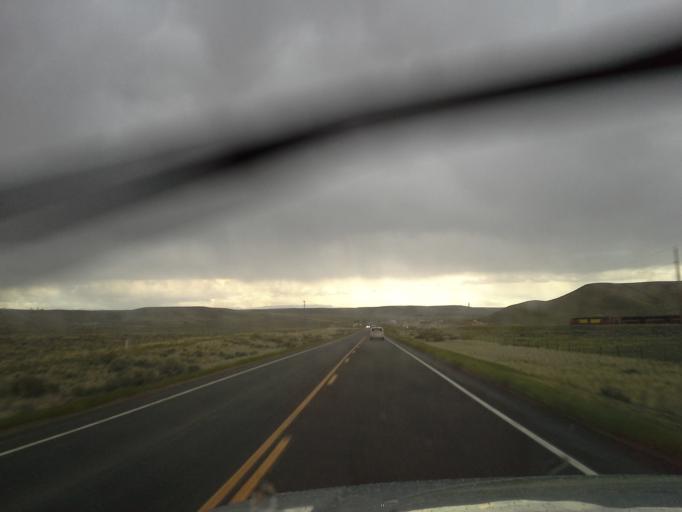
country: US
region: Wyoming
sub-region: Park County
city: Powell
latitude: 45.0664
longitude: -108.6718
